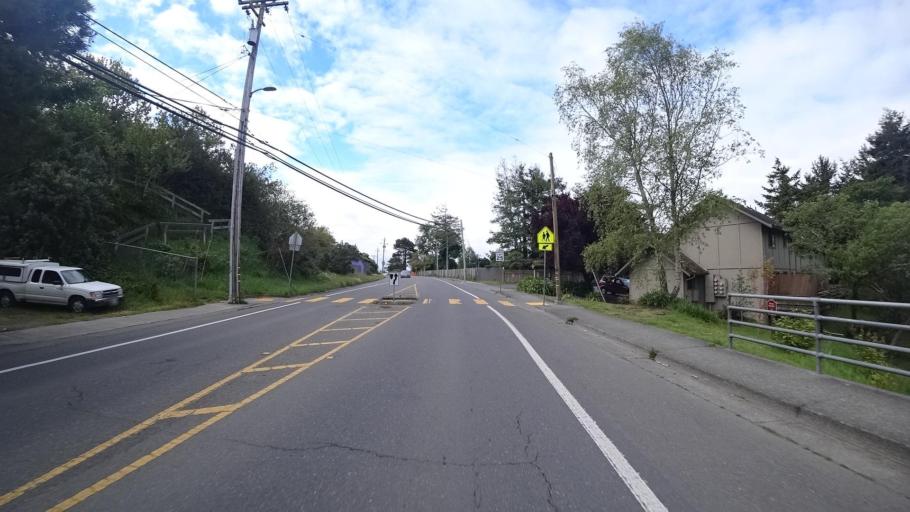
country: US
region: California
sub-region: Humboldt County
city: Arcata
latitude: 40.8820
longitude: -124.0917
